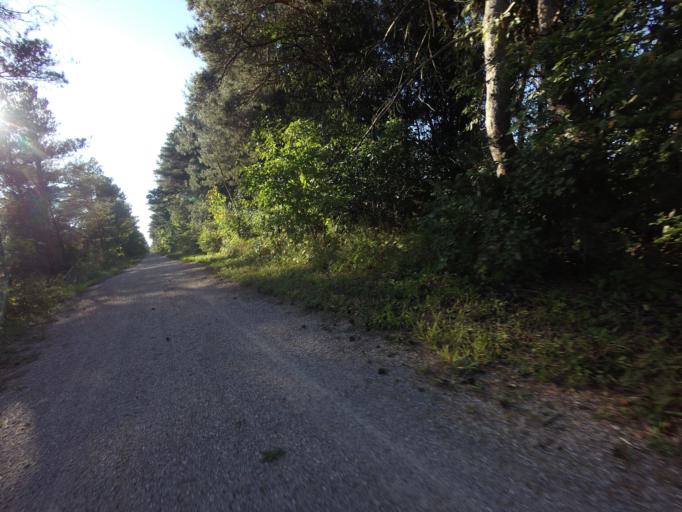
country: CA
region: Ontario
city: Goderich
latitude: 43.7527
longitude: -81.5952
